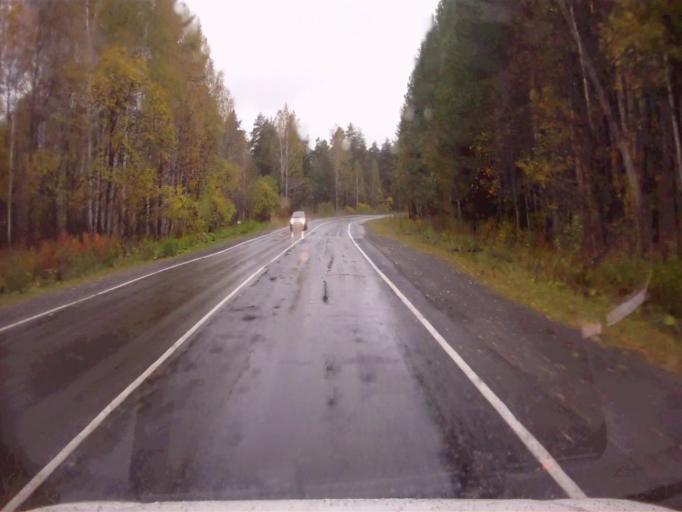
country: RU
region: Chelyabinsk
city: Verkhniy Ufaley
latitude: 55.9592
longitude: 60.3850
